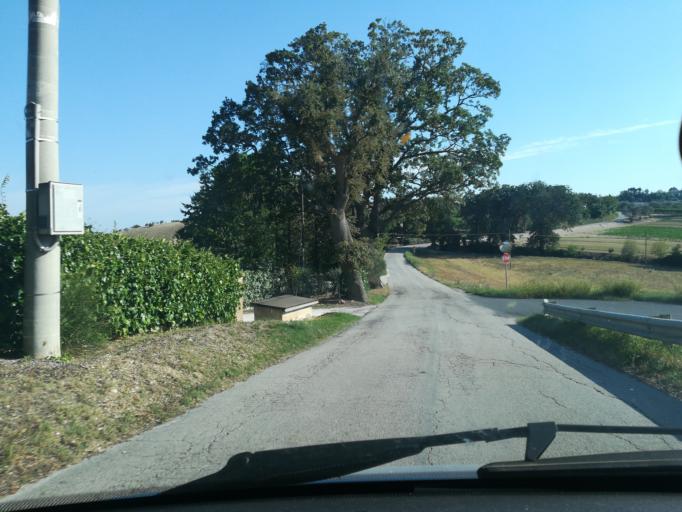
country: IT
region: The Marches
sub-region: Provincia di Macerata
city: Piediripa
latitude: 43.3027
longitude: 13.4790
